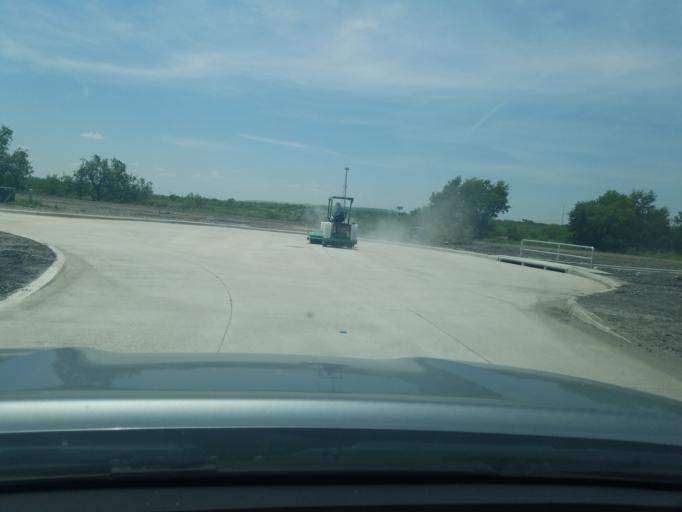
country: US
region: Texas
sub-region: Bexar County
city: Converse
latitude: 29.4633
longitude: -98.3257
